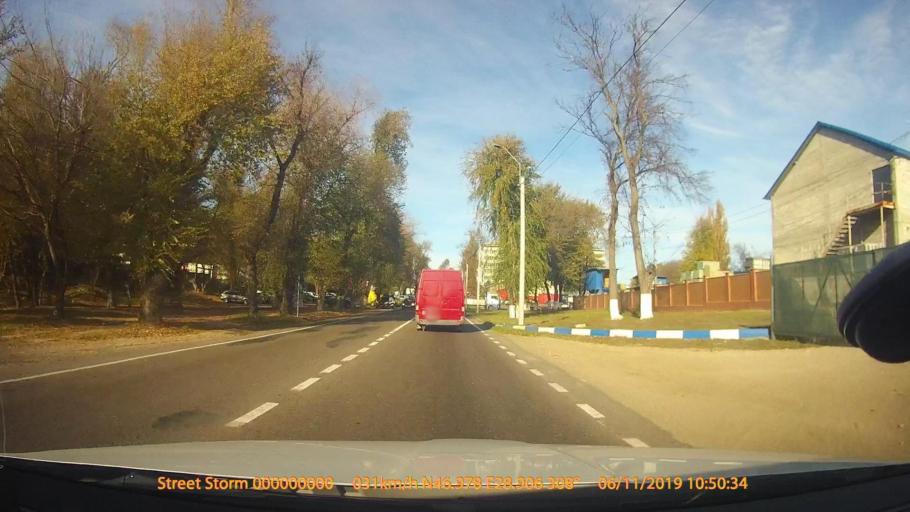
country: MD
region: Chisinau
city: Chisinau
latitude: 46.9777
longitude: 28.9063
